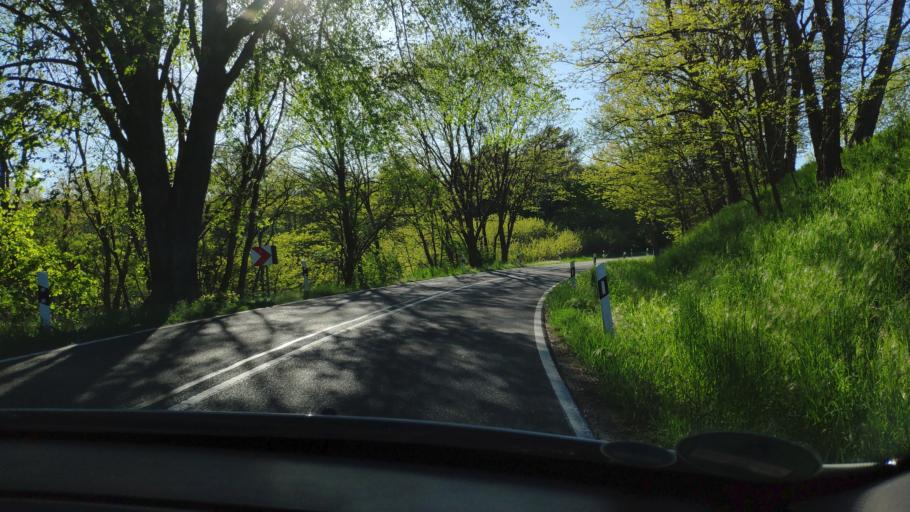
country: DE
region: Mecklenburg-Vorpommern
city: Wesenberg
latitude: 53.3199
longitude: 12.9619
